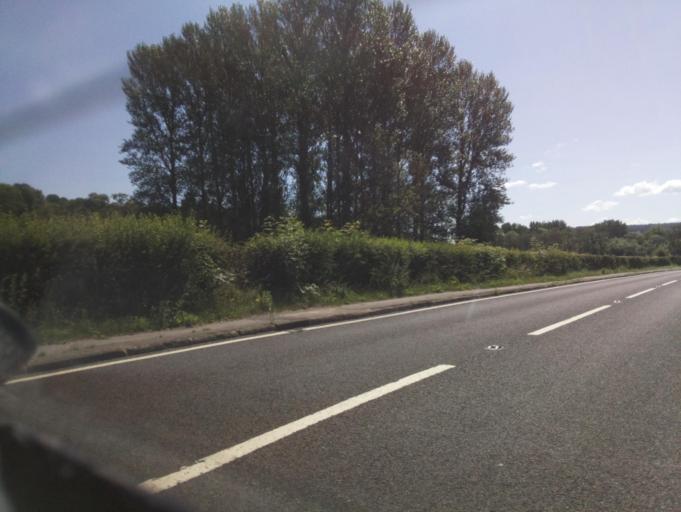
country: GB
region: England
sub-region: Derbyshire
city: Bakewell
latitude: 53.1995
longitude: -1.6613
